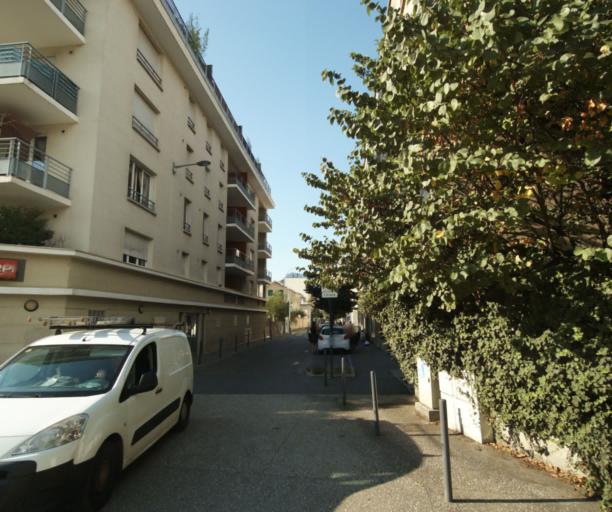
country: FR
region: Rhone-Alpes
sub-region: Departement de l'Isere
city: Seyssinet-Pariset
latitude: 45.1892
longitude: 5.6973
